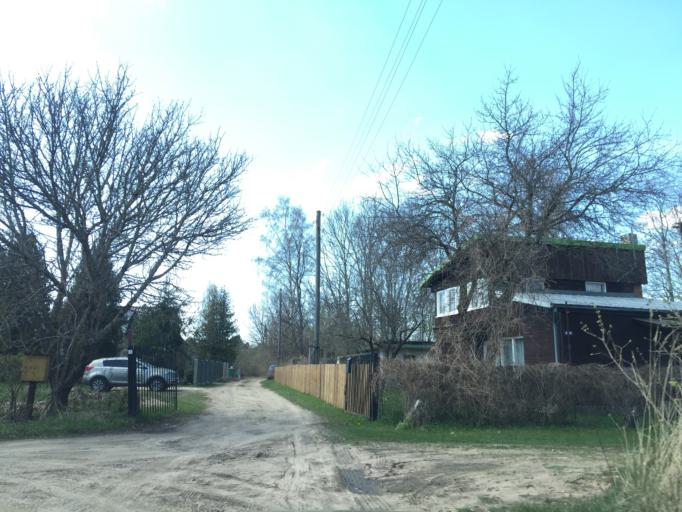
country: LV
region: Saulkrastu
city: Saulkrasti
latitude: 57.2391
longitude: 24.4504
